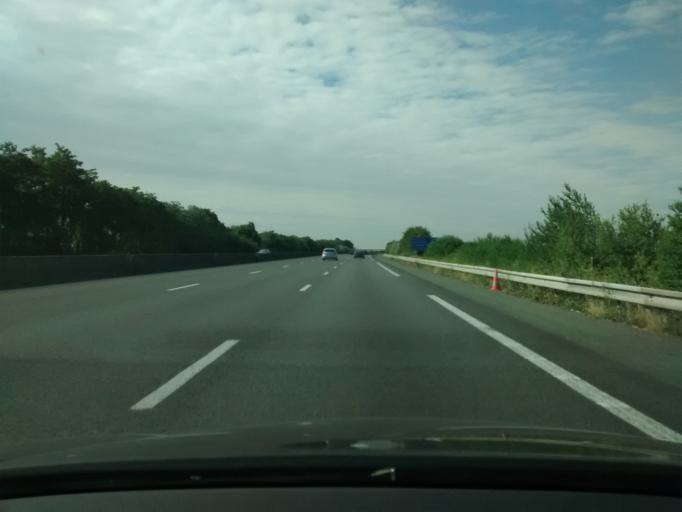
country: FR
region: Ile-de-France
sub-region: Departement de l'Essonne
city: Corbreuse
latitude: 48.4495
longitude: 1.9106
